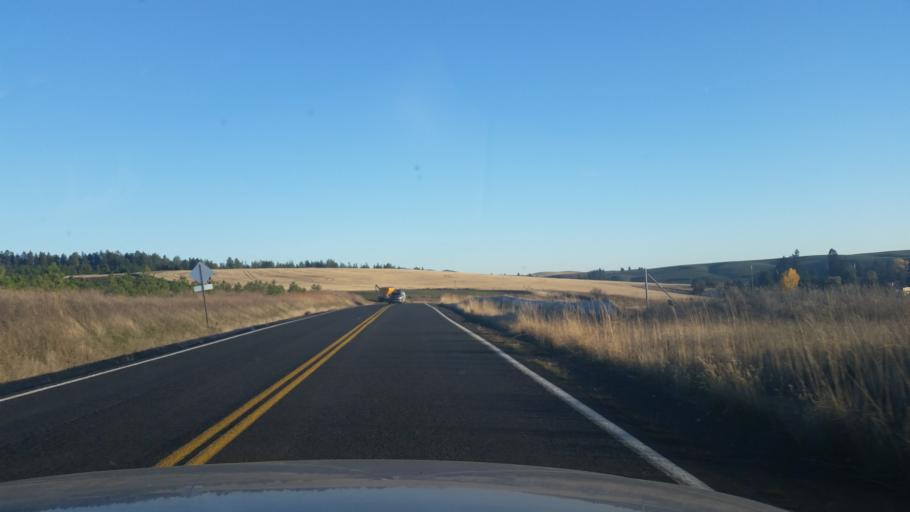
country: US
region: Washington
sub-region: Spokane County
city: Opportunity
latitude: 47.3491
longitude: -117.2294
